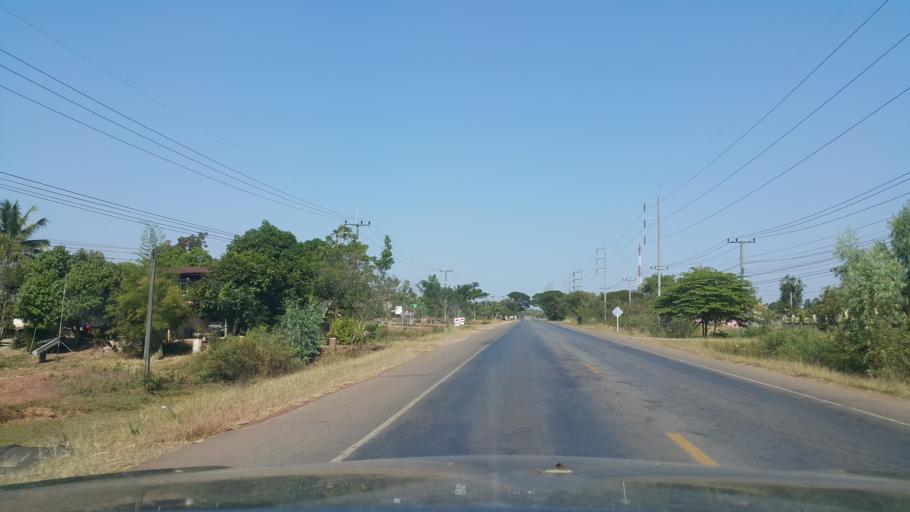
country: TH
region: Changwat Udon Thani
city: Thung Fon
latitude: 17.5032
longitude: 103.2035
